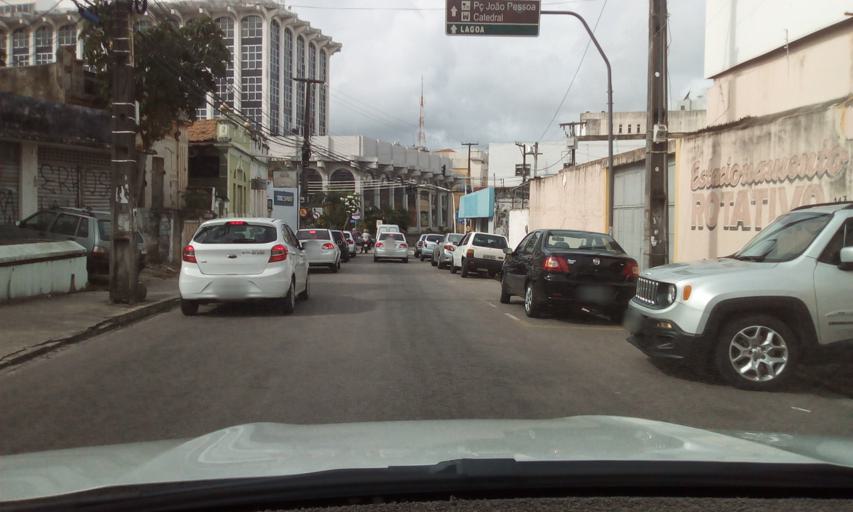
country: BR
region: Paraiba
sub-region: Joao Pessoa
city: Joao Pessoa
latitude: -7.1236
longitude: -34.8835
